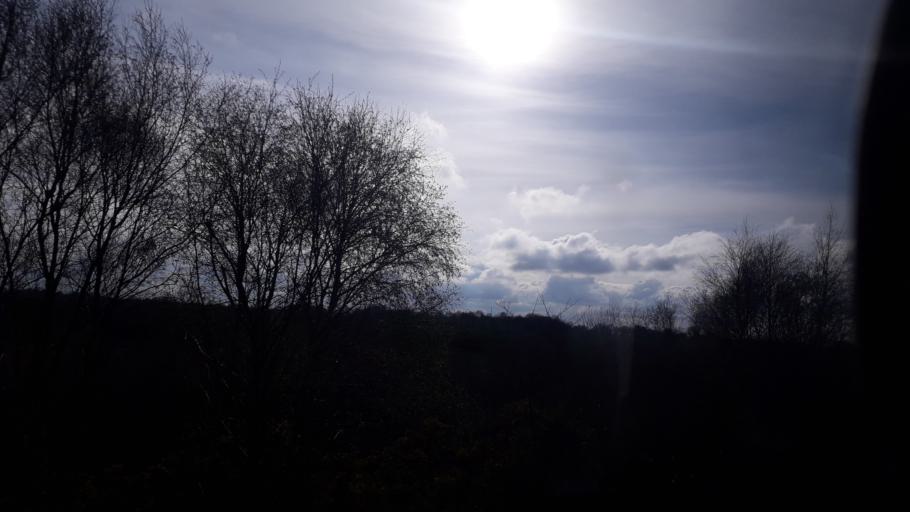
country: IE
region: Leinster
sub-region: An Mhi
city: Ballivor
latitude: 53.4713
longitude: -6.9928
